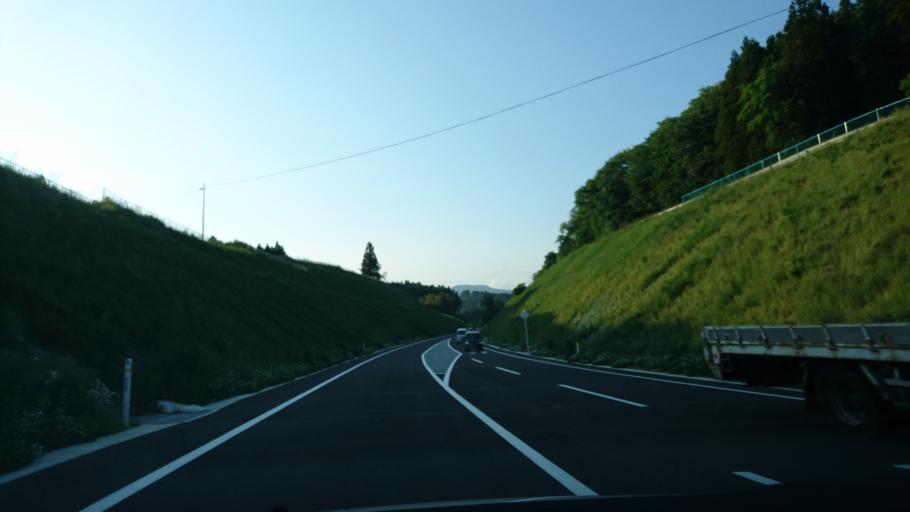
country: JP
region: Iwate
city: Ofunato
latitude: 38.9201
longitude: 141.4564
